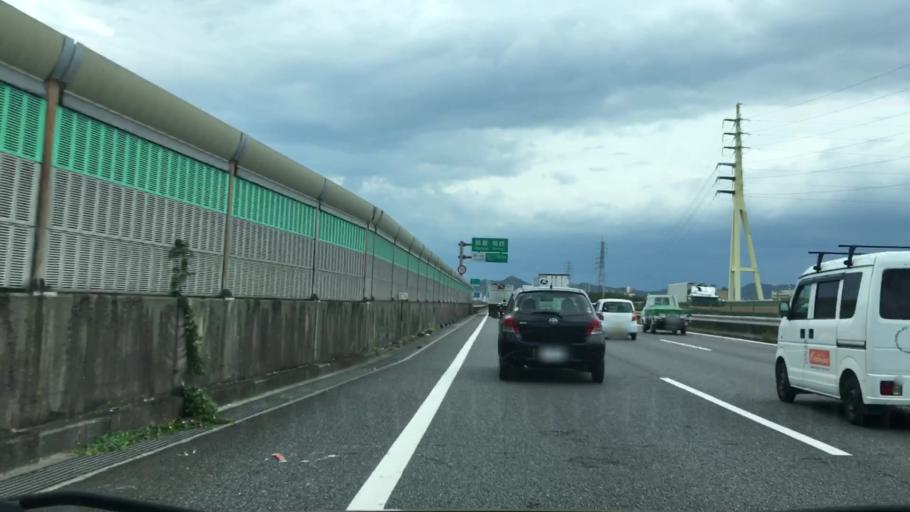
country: JP
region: Hyogo
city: Himeji
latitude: 34.8066
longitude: 134.6986
